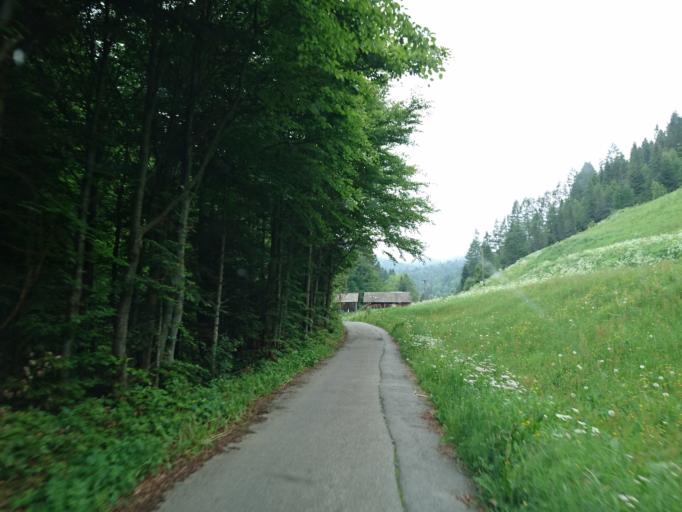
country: PL
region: Lesser Poland Voivodeship
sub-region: Powiat limanowski
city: Lubomierz
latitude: 49.5347
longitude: 20.2057
